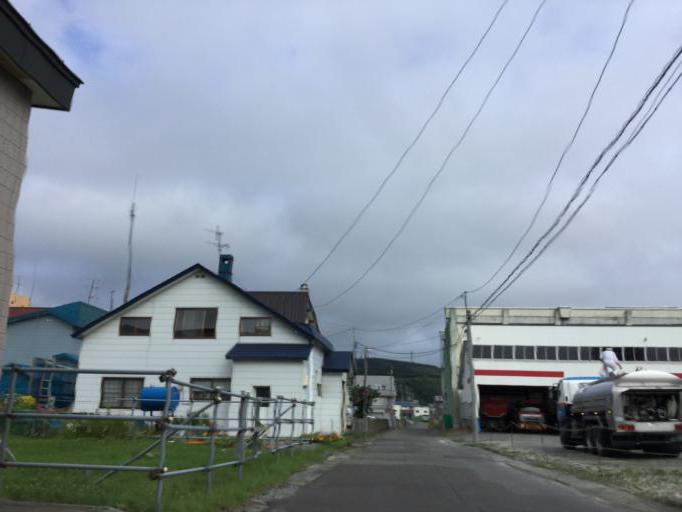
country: JP
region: Hokkaido
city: Wakkanai
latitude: 45.4005
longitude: 141.6843
